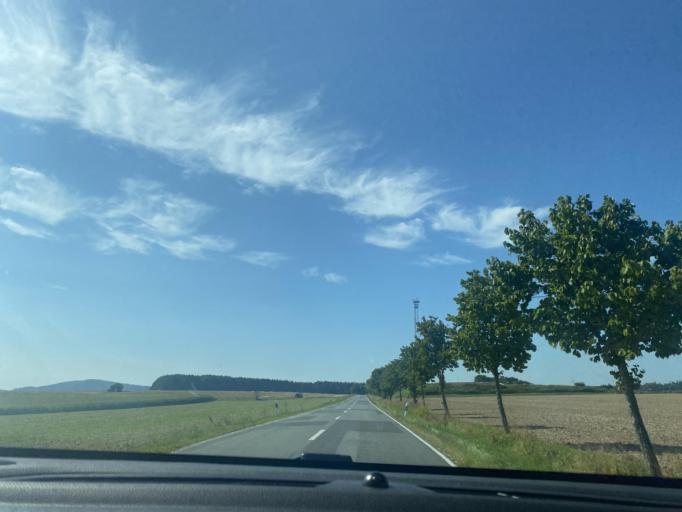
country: DE
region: Saxony
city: Grosshennersdorf
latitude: 51.0141
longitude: 14.7983
